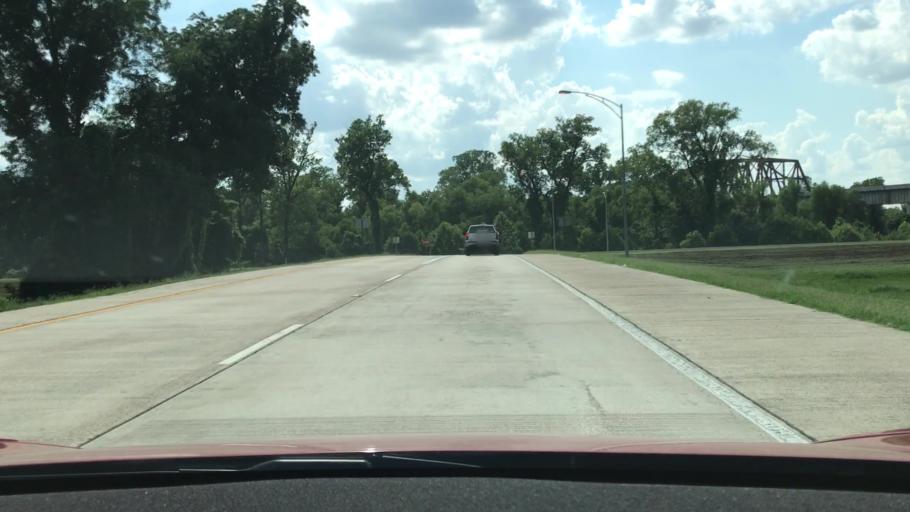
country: US
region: Louisiana
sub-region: Bossier Parish
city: Bossier City
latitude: 32.4577
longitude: -93.6742
